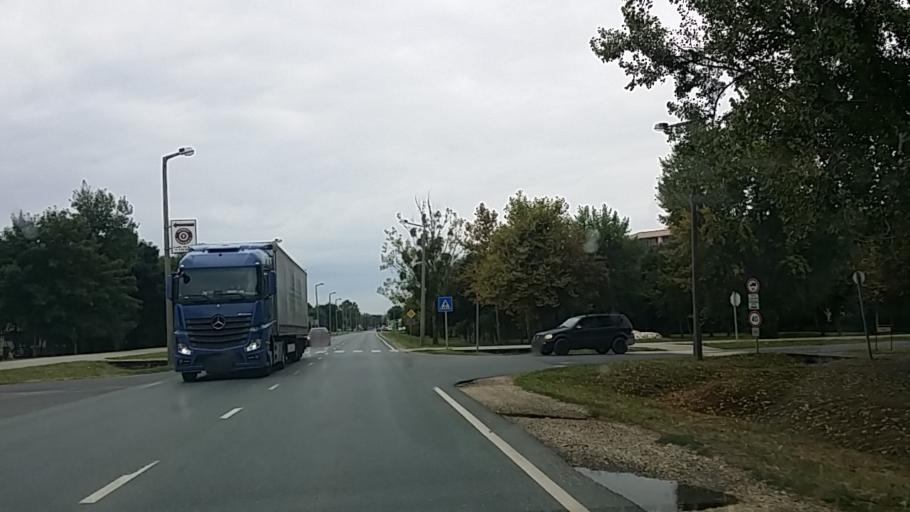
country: HU
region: Gyor-Moson-Sopron
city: Kapuvar
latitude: 47.5915
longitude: 17.0399
